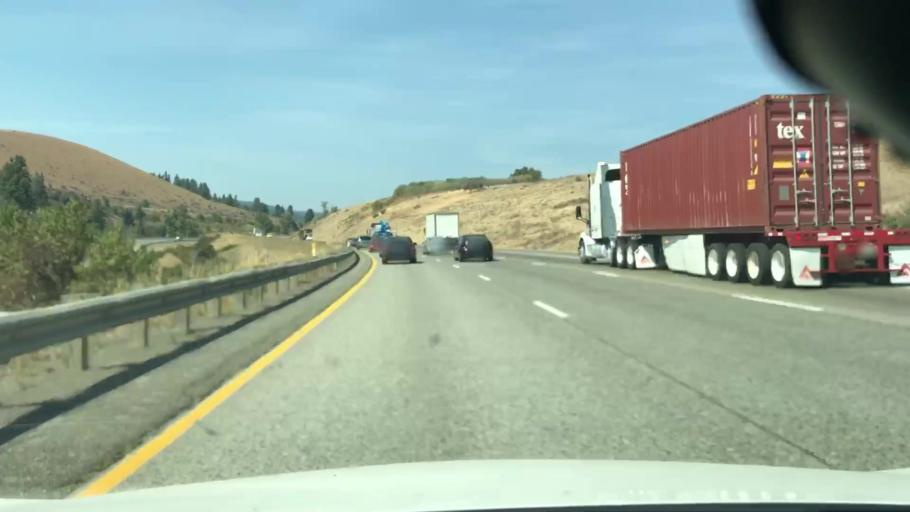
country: US
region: Washington
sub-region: Kittitas County
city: Ellensburg
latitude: 47.0877
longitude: -120.7467
